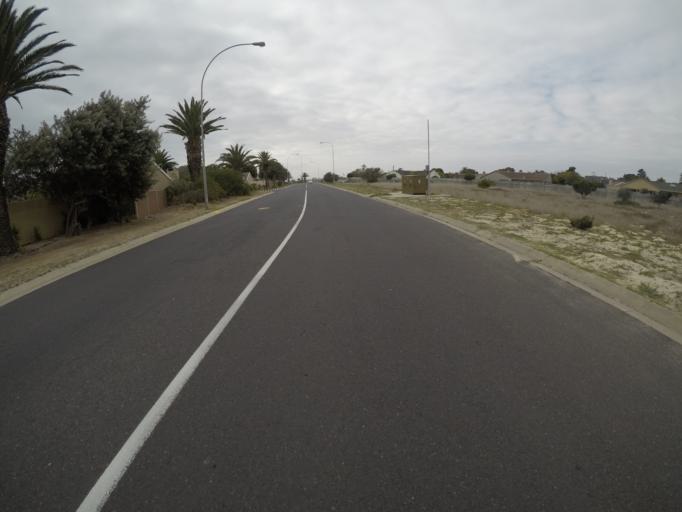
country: ZA
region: Western Cape
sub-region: City of Cape Town
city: Atlantis
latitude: -33.6967
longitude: 18.4443
